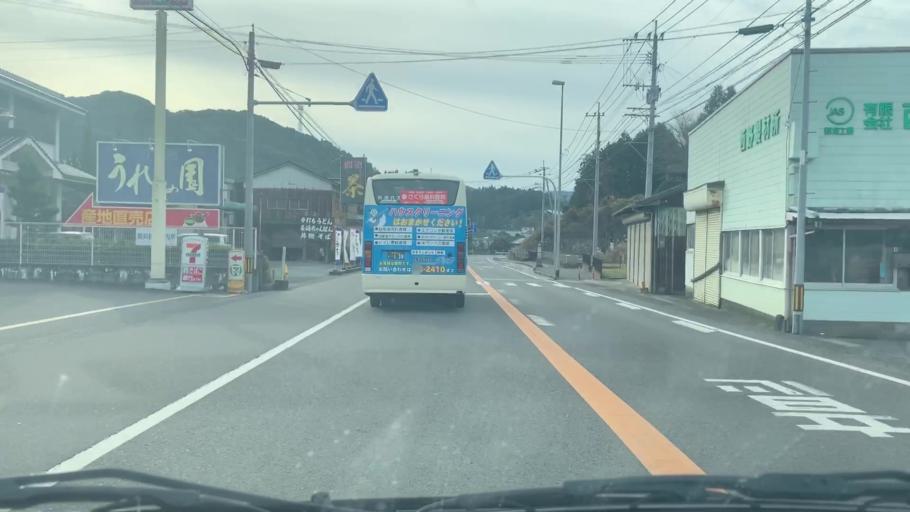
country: JP
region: Saga Prefecture
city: Ureshinomachi-shimojuku
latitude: 33.1184
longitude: 130.0012
